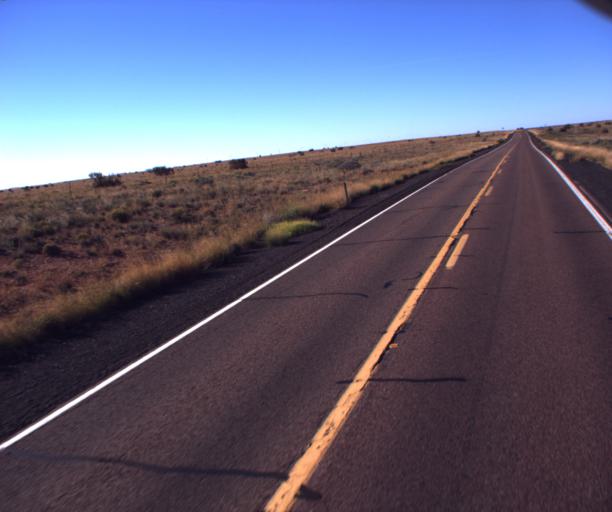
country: US
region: Arizona
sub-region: Navajo County
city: Holbrook
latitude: 34.7615
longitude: -110.2483
